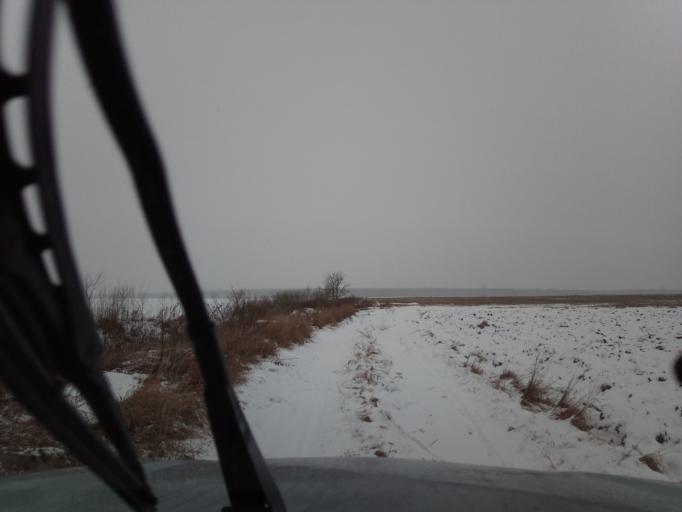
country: LT
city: Ramygala
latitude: 55.4837
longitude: 24.2936
